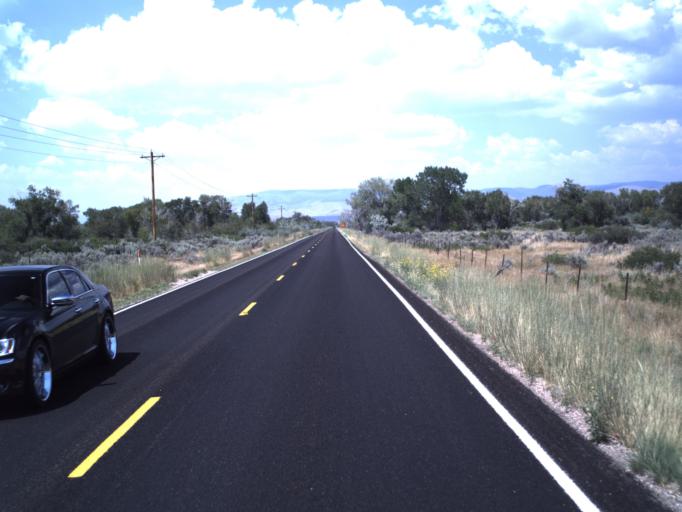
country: US
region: Utah
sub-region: Duchesne County
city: Roosevelt
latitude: 40.4179
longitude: -109.9201
